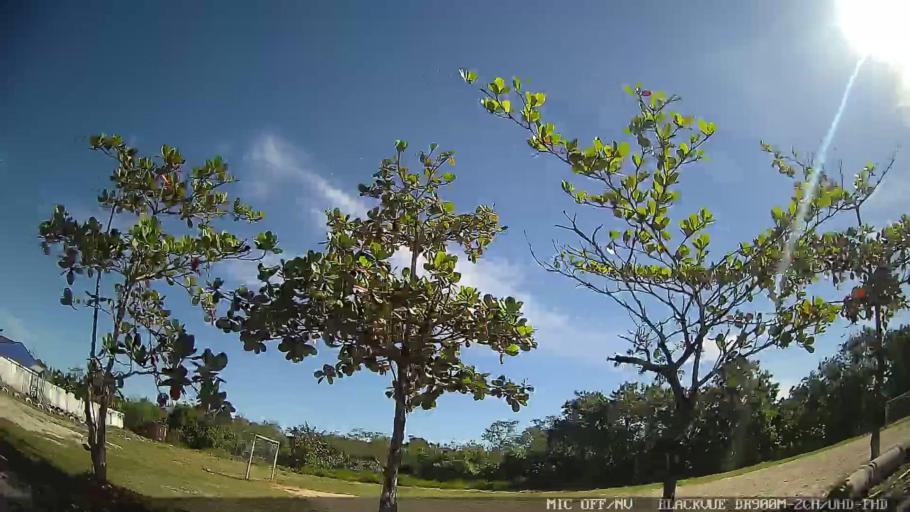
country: BR
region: Sao Paulo
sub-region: Santos
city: Santos
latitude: -23.9349
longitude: -46.2894
